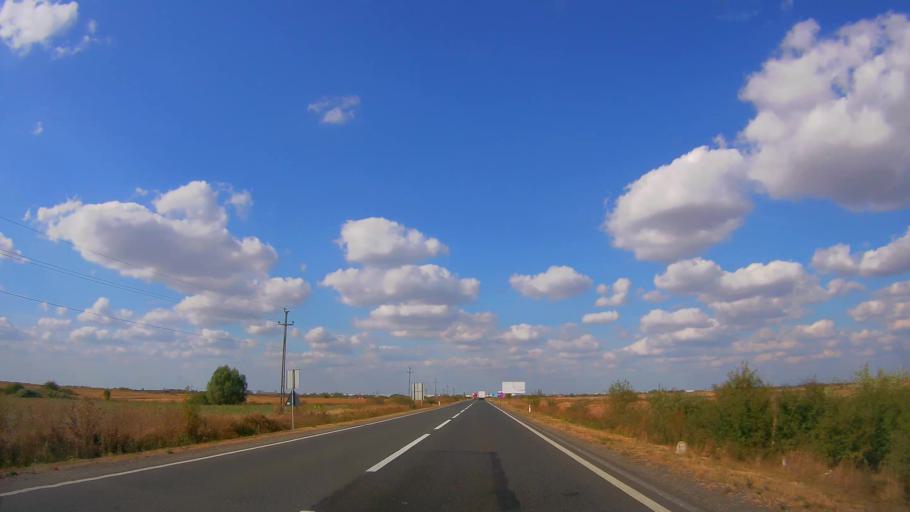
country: RO
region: Satu Mare
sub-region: Oras Ardud
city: Madaras
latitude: 47.7102
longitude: 22.8722
